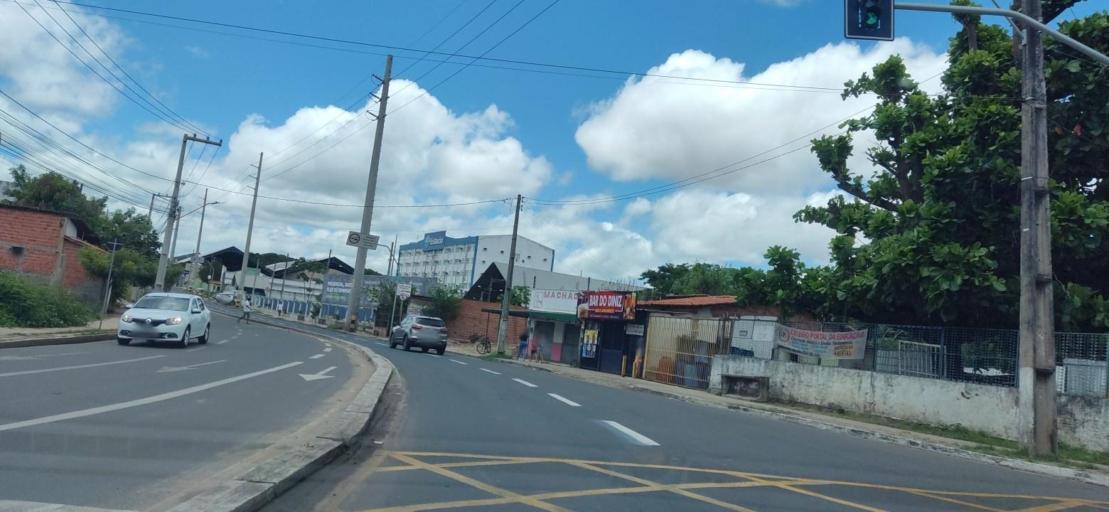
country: BR
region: Piaui
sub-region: Teresina
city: Teresina
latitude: -5.0867
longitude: -42.7657
